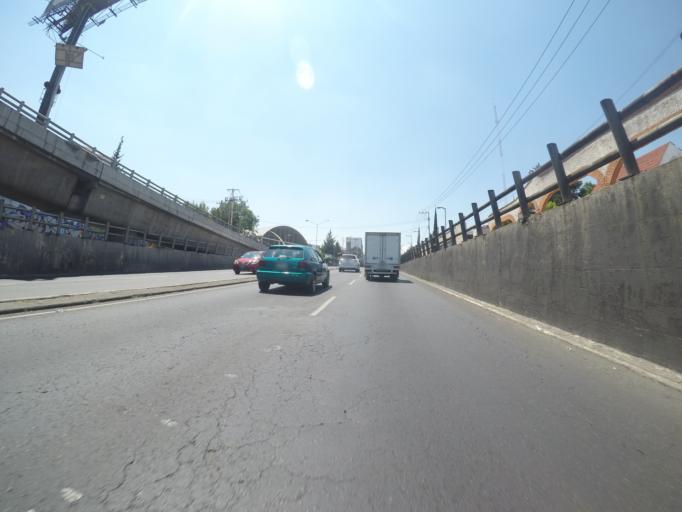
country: MX
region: Mexico City
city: Polanco
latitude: 19.4102
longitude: -99.1952
